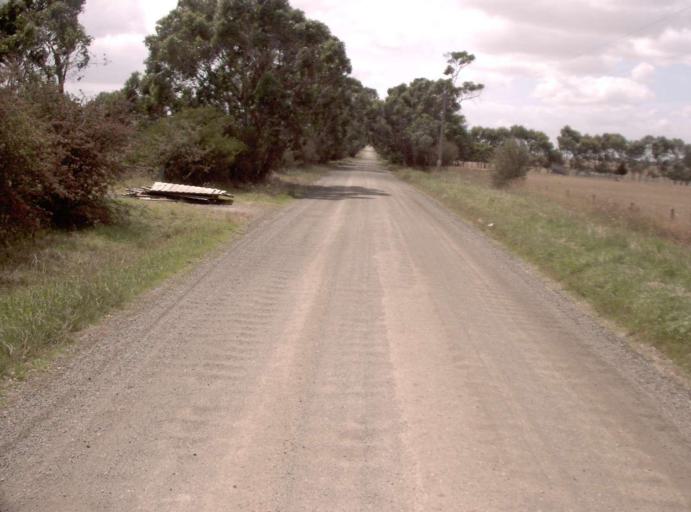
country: AU
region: Victoria
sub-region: Casey
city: Cranbourne East
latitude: -38.0897
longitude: 145.3361
